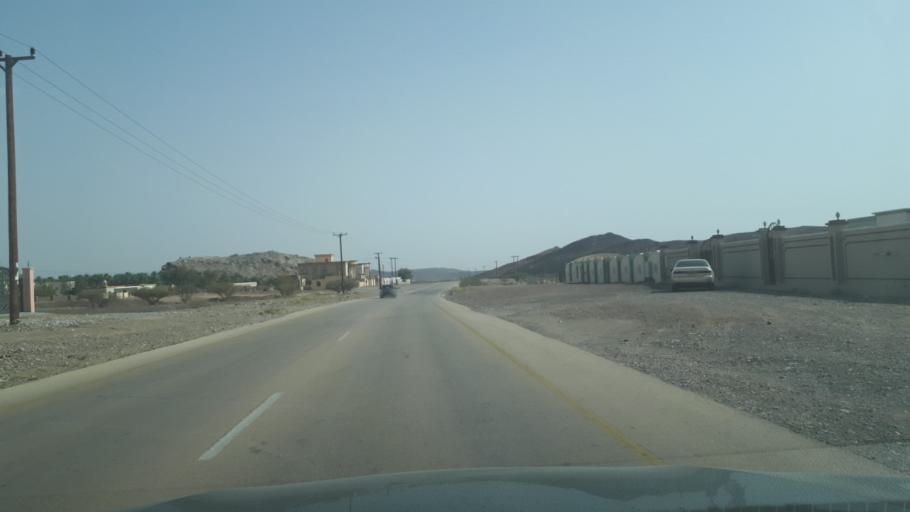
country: OM
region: Az Zahirah
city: `Ibri
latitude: 23.1585
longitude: 56.9116
